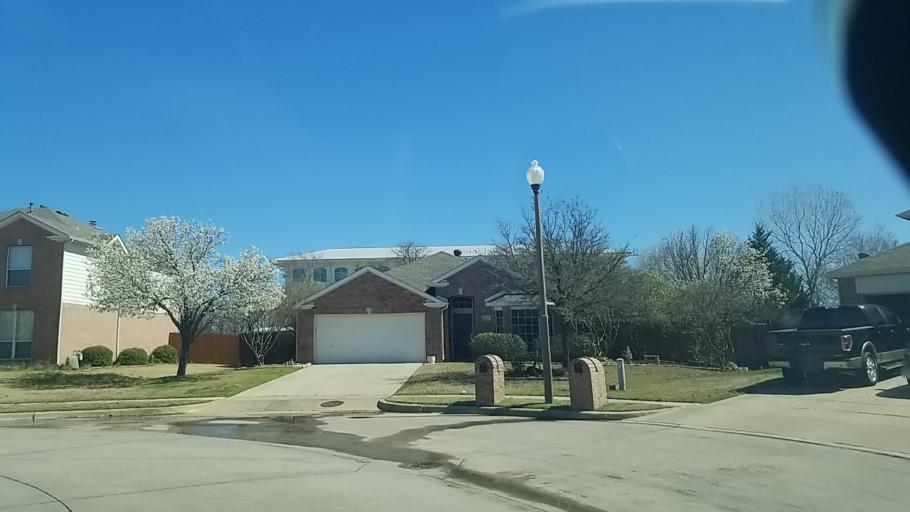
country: US
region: Texas
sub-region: Denton County
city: Corinth
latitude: 33.1743
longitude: -97.1020
